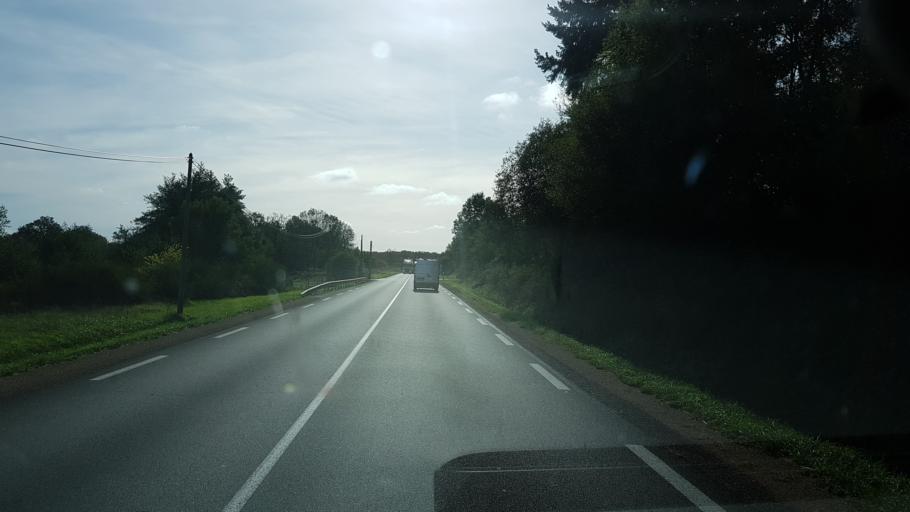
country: FR
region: Limousin
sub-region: Departement de la Haute-Vienne
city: Bellac
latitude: 46.1485
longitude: 1.1038
